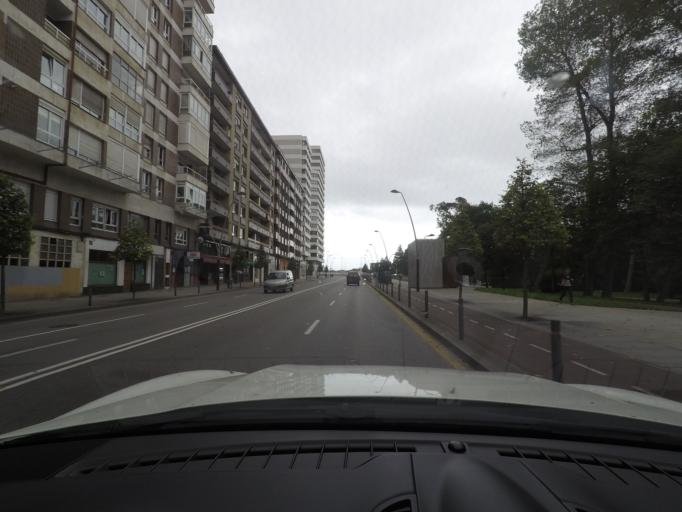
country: ES
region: Asturias
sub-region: Province of Asturias
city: Gijon
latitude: 43.5386
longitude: -5.6461
